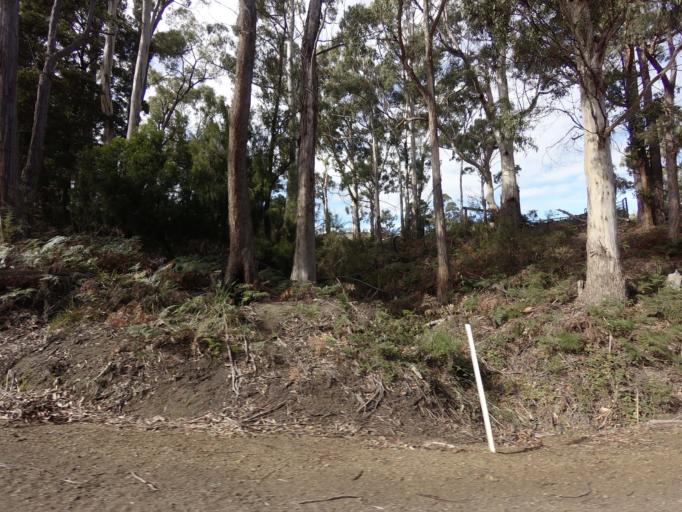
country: AU
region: Tasmania
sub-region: Clarence
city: Sandford
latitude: -43.0889
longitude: 147.7154
